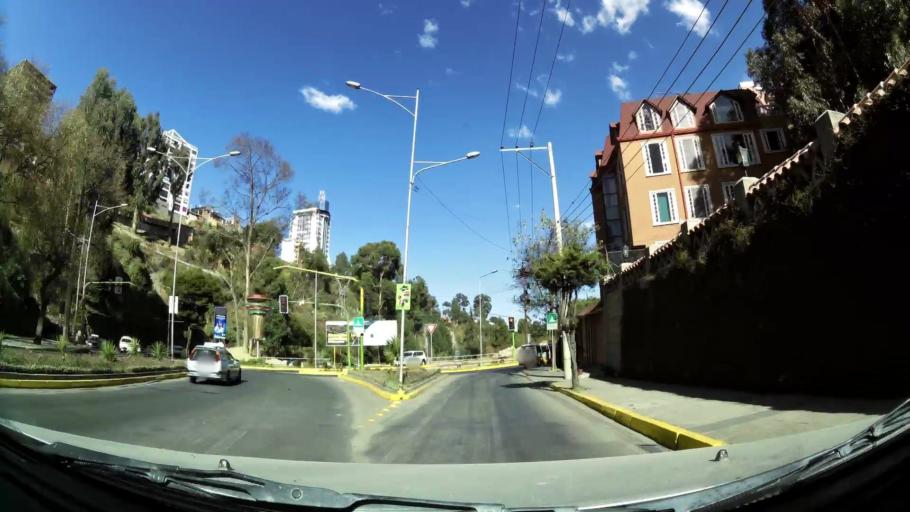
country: BO
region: La Paz
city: La Paz
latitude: -16.5122
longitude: -68.1197
